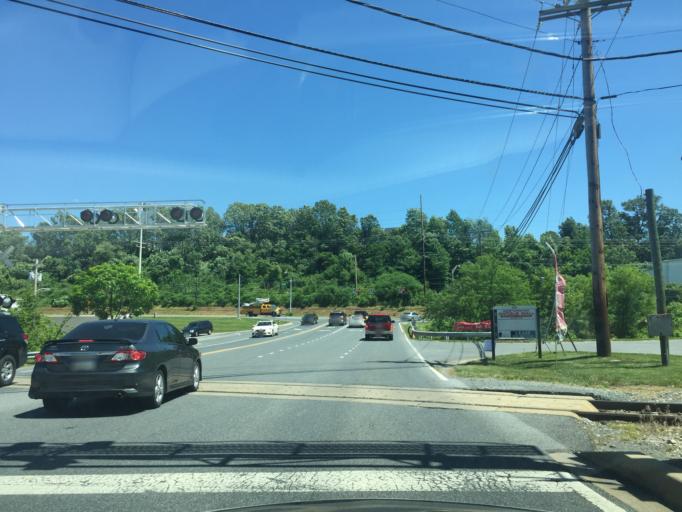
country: US
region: Maryland
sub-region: Carroll County
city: Westminster
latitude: 39.5847
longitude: -76.9804
